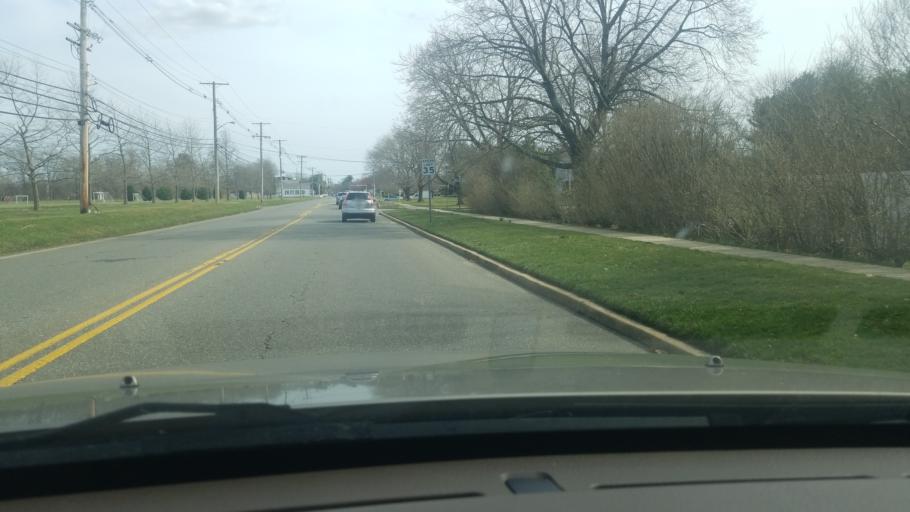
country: US
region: New Jersey
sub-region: Monmouth County
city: West Freehold
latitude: 40.2450
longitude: -74.3049
